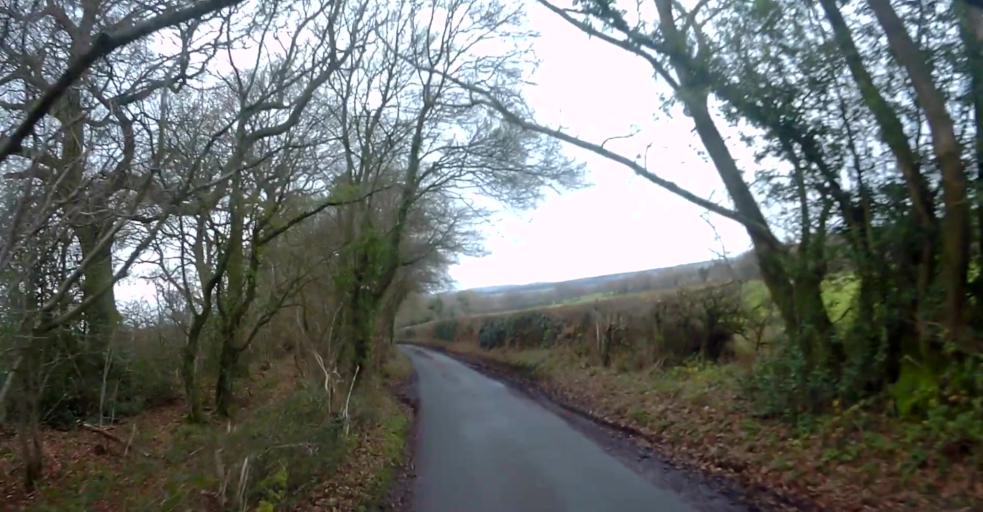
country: GB
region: England
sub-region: Hampshire
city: Overton
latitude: 51.2319
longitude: -1.2459
